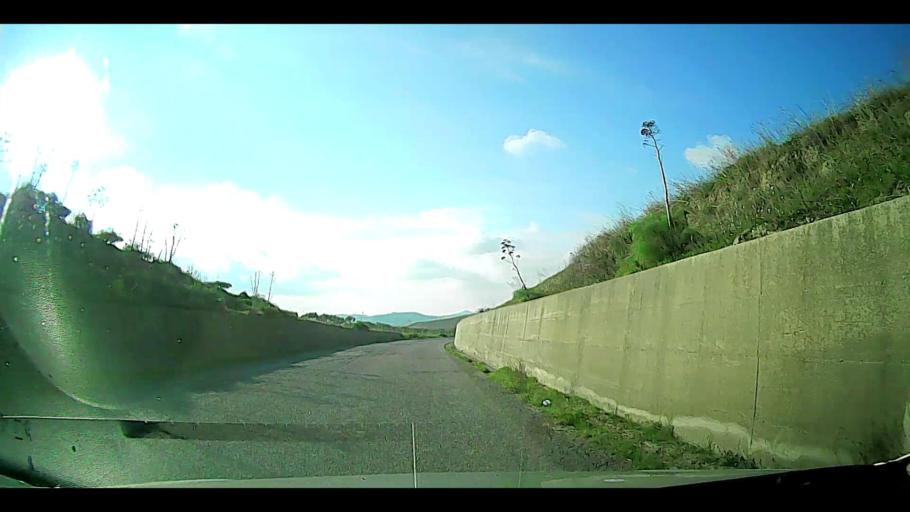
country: IT
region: Calabria
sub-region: Provincia di Crotone
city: Rocca di Neto
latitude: 39.1914
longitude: 17.0584
